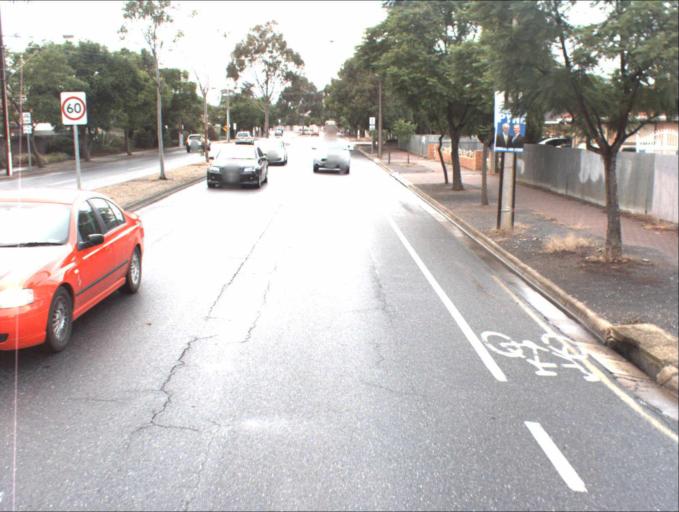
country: AU
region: South Australia
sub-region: Norwood Payneham St Peters
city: Marden
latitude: -34.8889
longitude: 138.6396
